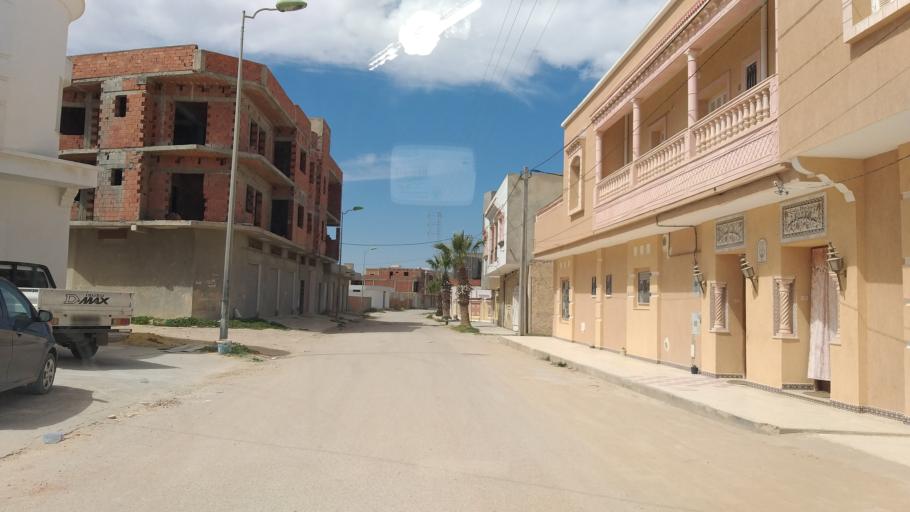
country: TN
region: Al Mahdiyah
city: El Jem
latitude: 35.3016
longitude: 10.6992
